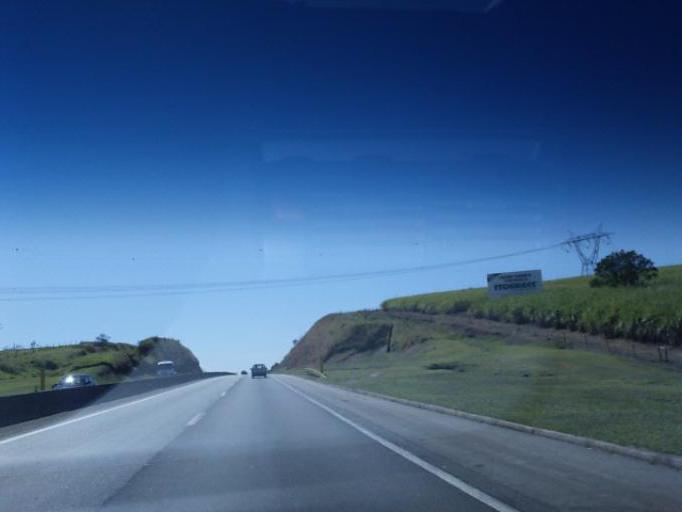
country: BR
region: Sao Paulo
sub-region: Cacapava
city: Cacapava
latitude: -23.0824
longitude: -45.6622
